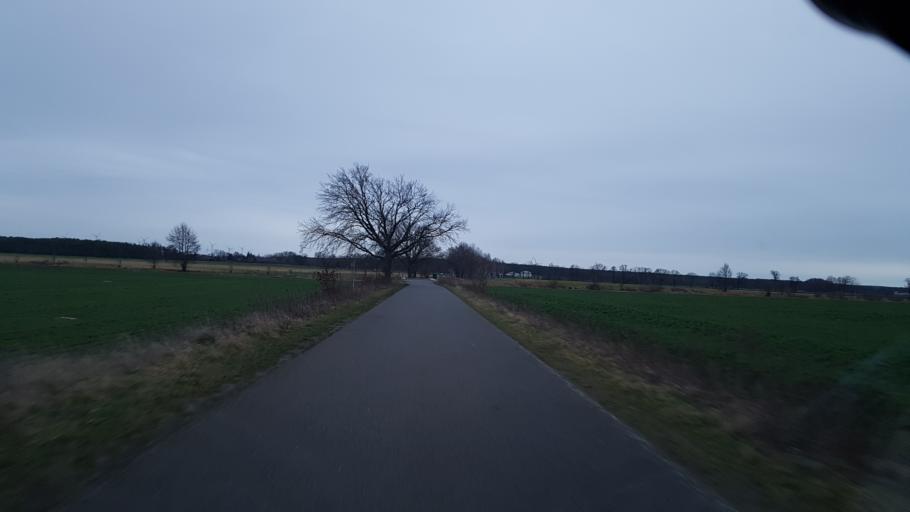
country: DE
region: Brandenburg
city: Schlieben
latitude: 51.7039
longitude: 13.3202
